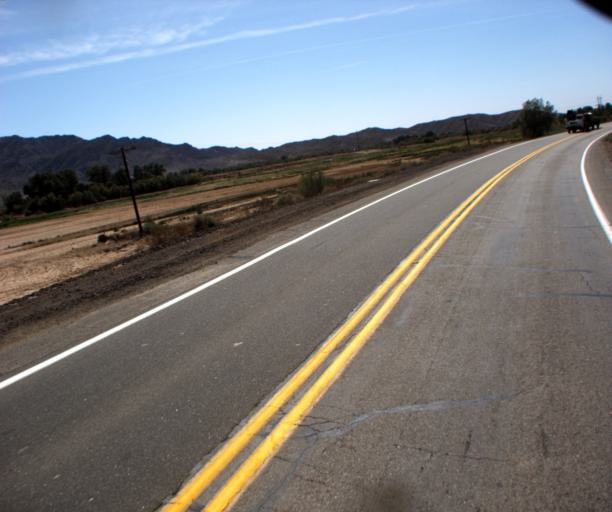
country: US
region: Arizona
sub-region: Yuma County
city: Fortuna Foothills
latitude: 32.7707
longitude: -114.3897
